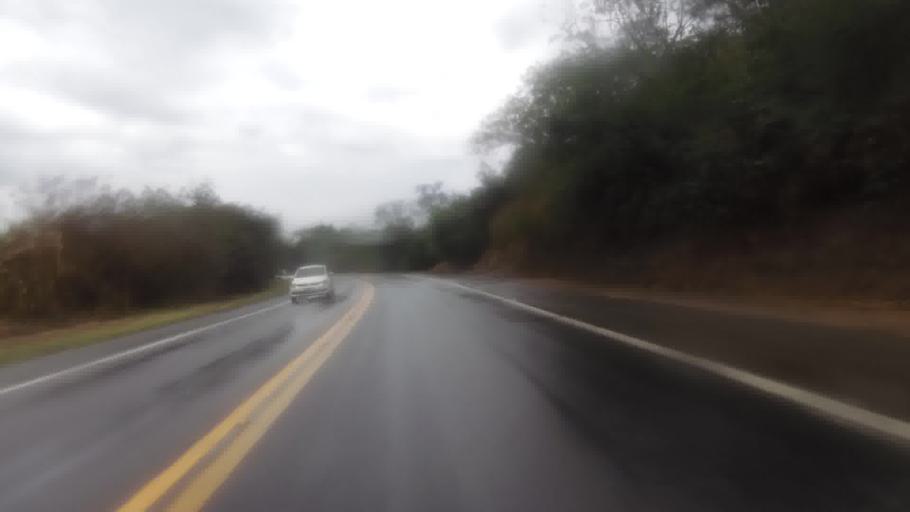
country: BR
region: Espirito Santo
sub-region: Cachoeiro De Itapemirim
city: Cachoeiro de Itapemirim
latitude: -21.0124
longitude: -41.1473
